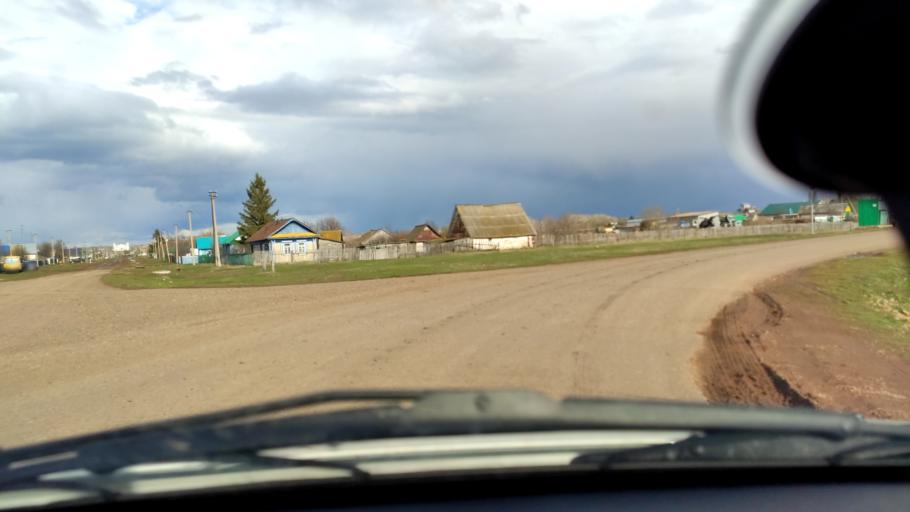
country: RU
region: Bashkortostan
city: Buzdyak
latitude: 54.7678
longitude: 54.6000
